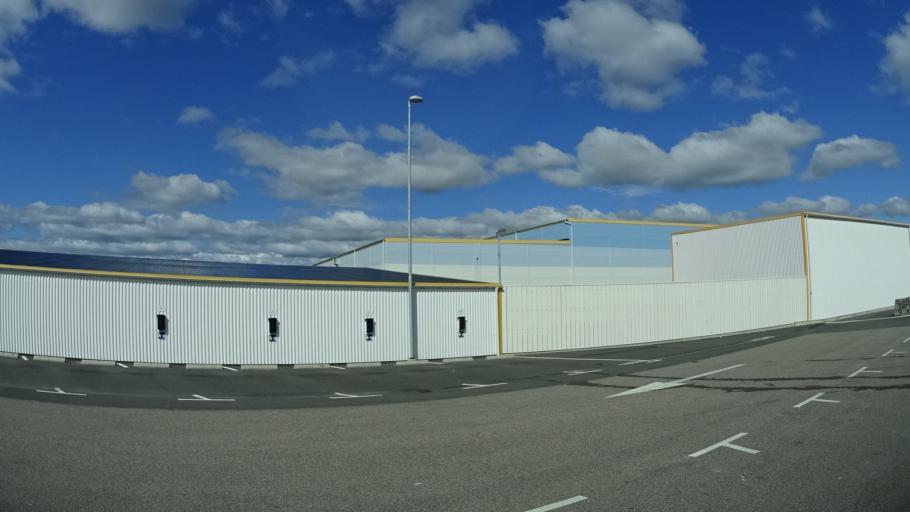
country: SE
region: Halland
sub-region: Halmstads Kommun
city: Getinge
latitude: 56.8555
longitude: 12.6824
